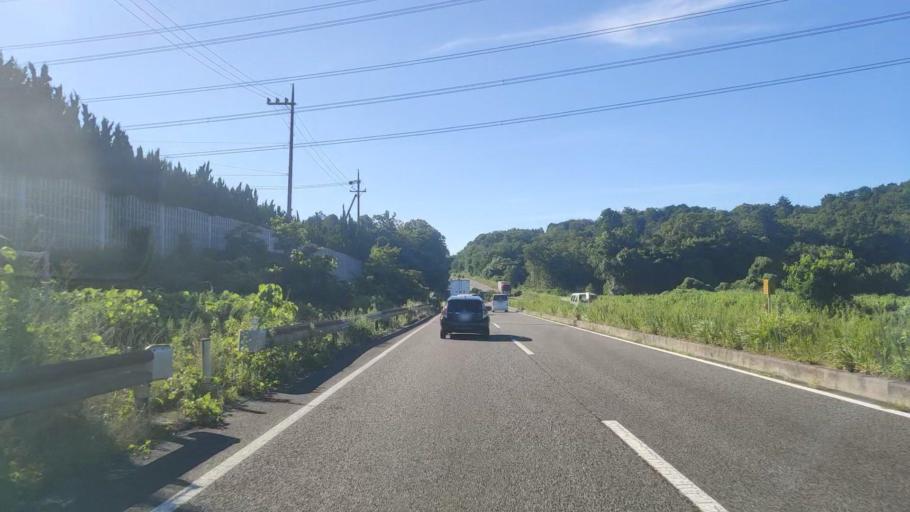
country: JP
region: Shiga Prefecture
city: Minakuchicho-matoba
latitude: 34.9676
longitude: 136.1950
